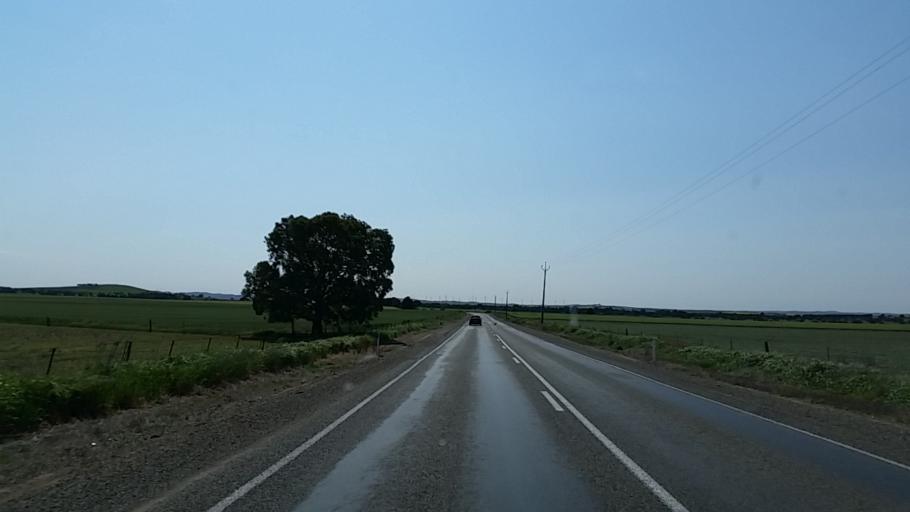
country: AU
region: South Australia
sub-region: Northern Areas
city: Jamestown
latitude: -33.1947
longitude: 138.4545
